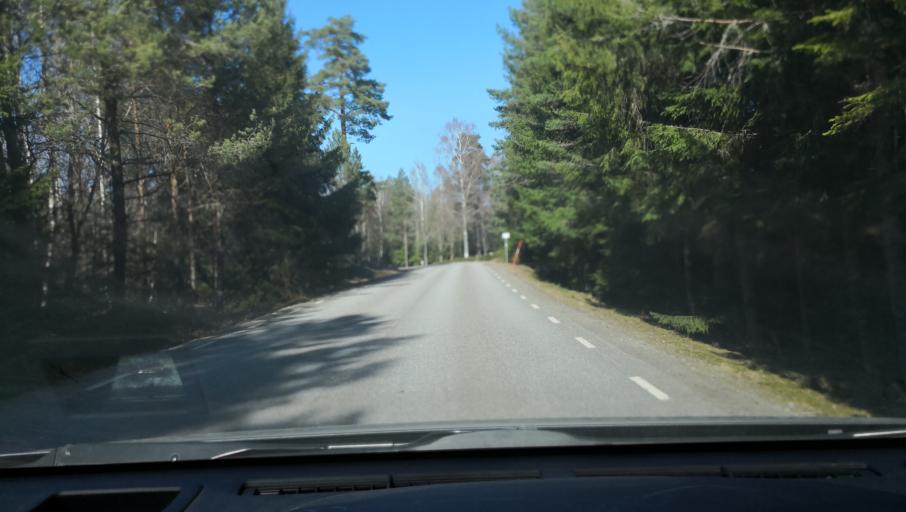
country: SE
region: Vaestmanland
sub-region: Sala Kommun
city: Sala
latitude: 60.0138
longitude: 16.5056
